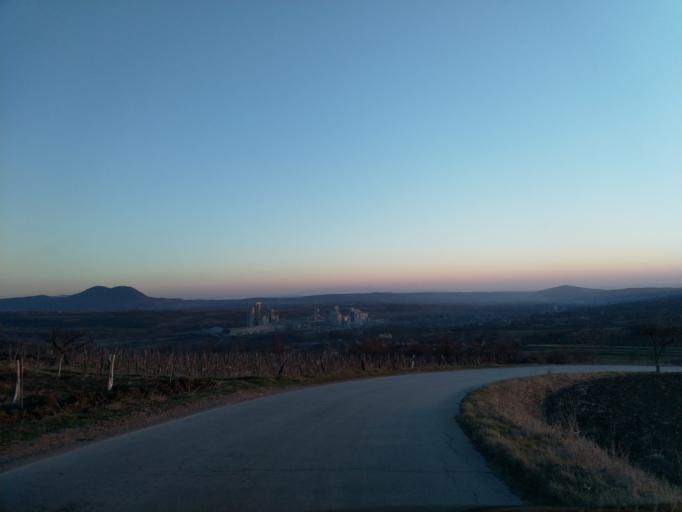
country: RS
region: Central Serbia
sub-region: Pomoravski Okrug
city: Paracin
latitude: 43.9249
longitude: 21.5115
